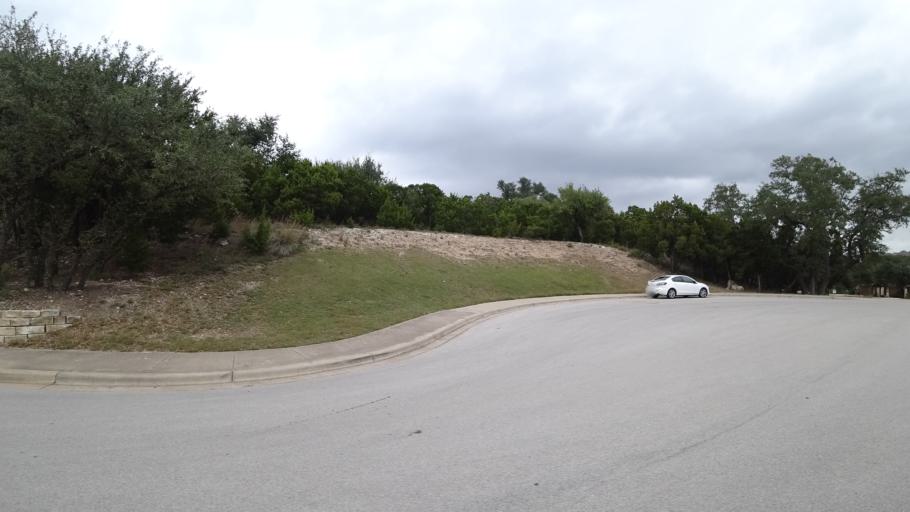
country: US
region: Texas
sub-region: Travis County
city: Bee Cave
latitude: 30.3436
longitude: -97.9149
